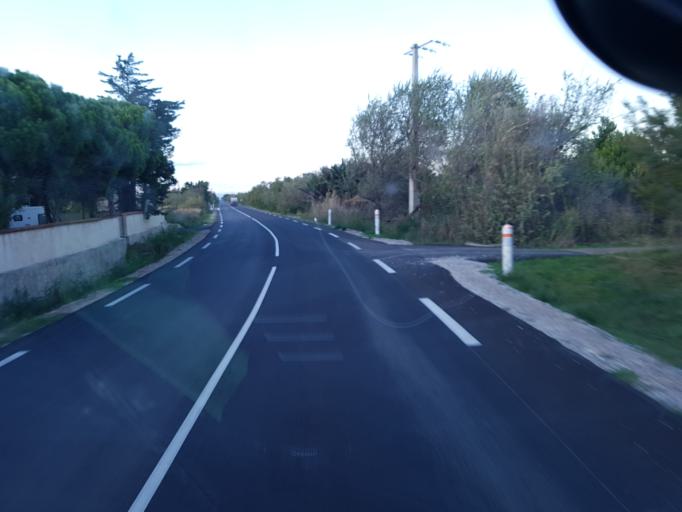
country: FR
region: Languedoc-Roussillon
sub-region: Departement de l'Aude
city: Port-la-Nouvelle
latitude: 42.9974
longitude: 3.0420
